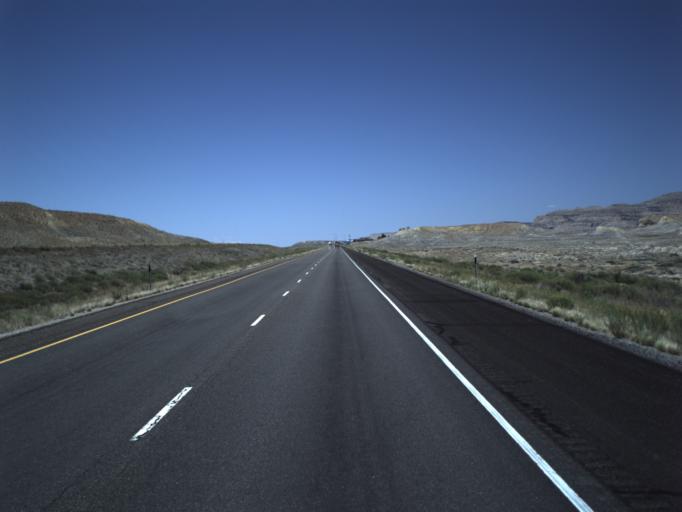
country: US
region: Utah
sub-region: Grand County
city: Moab
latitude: 38.9487
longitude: -109.6685
